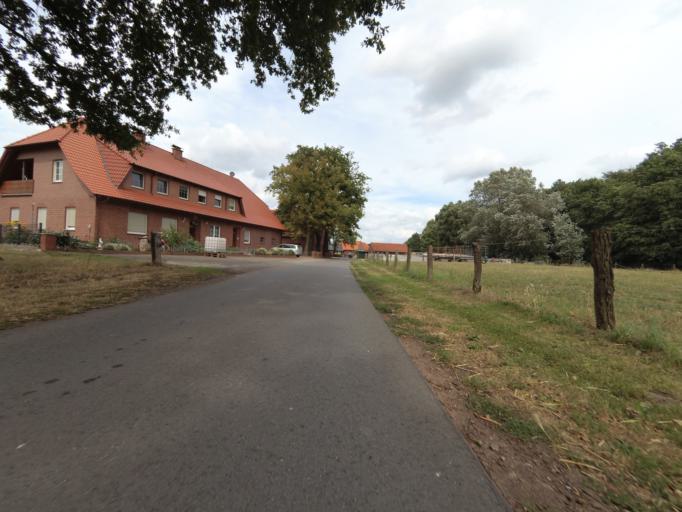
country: DE
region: North Rhine-Westphalia
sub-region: Regierungsbezirk Munster
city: Ahaus
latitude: 52.1177
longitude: 7.0149
